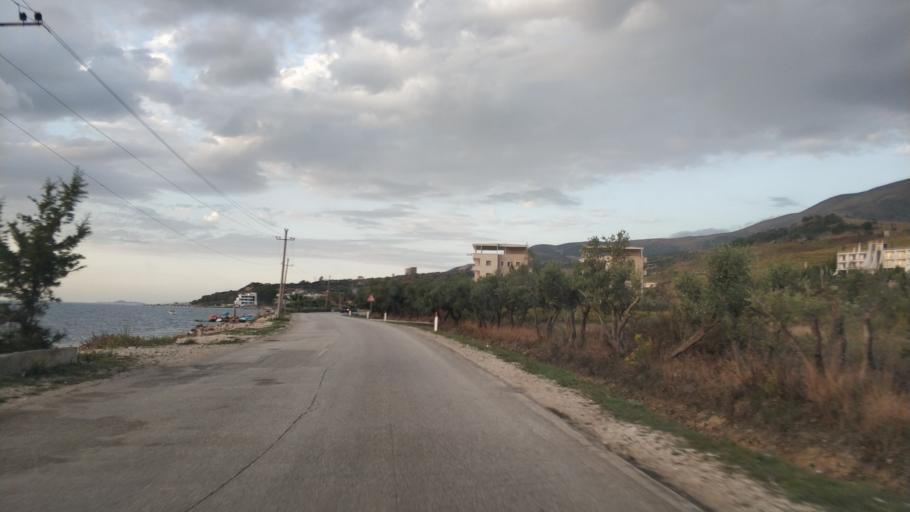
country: AL
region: Vlore
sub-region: Rrethi i Vlores
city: Orikum
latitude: 40.3483
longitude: 19.4856
